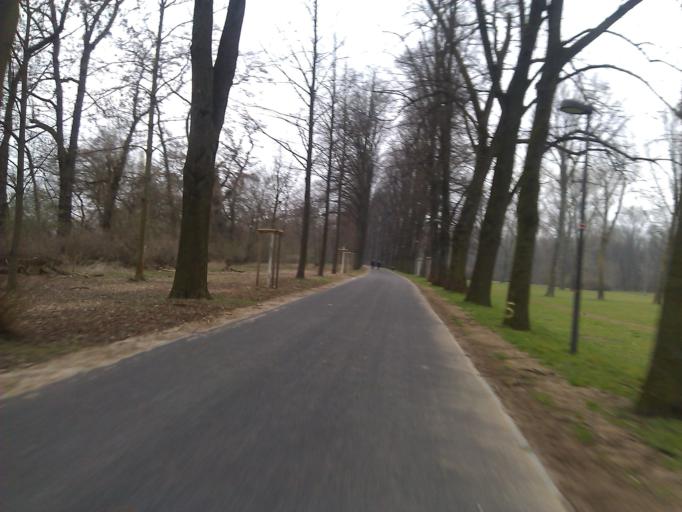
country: DE
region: North Rhine-Westphalia
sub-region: Regierungsbezirk Koln
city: Muelheim
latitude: 50.9696
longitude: 6.9923
